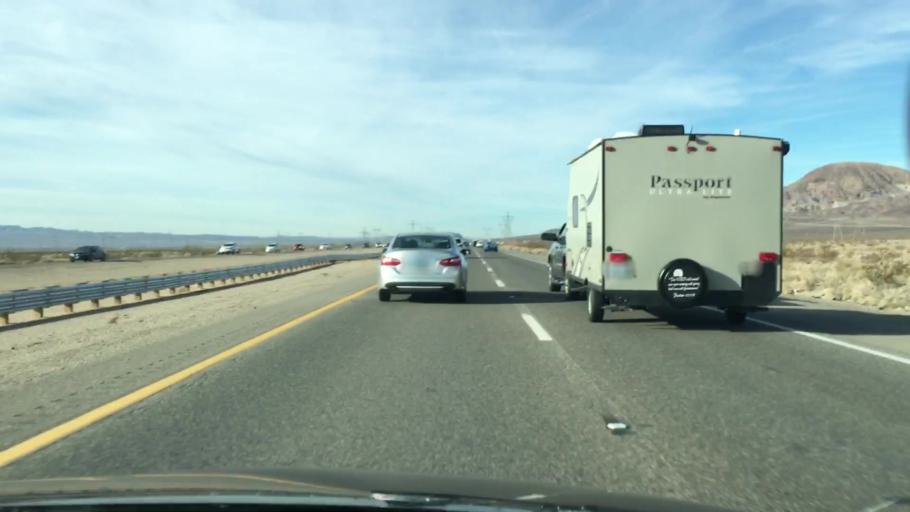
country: US
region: California
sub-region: San Bernardino County
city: Barstow
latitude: 34.9249
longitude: -116.7385
